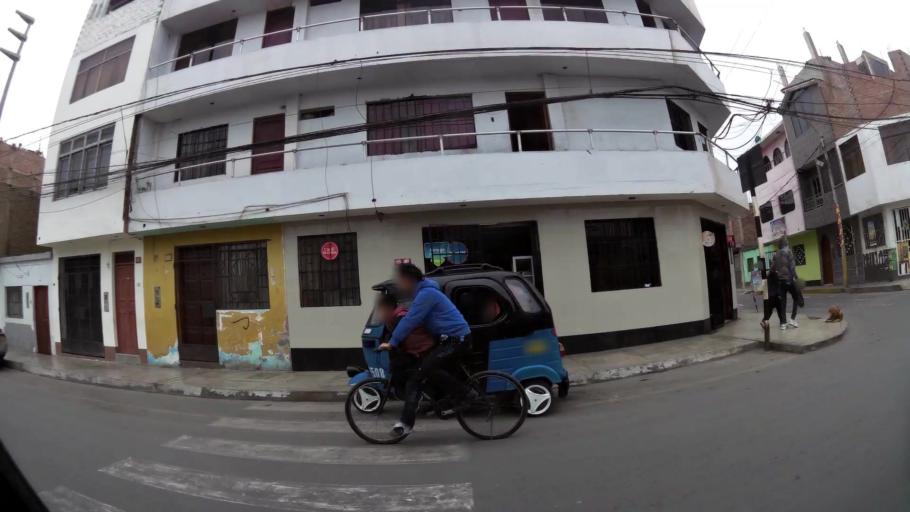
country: PE
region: Lima
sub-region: Barranca
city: Barranca
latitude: -10.7505
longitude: -77.7566
